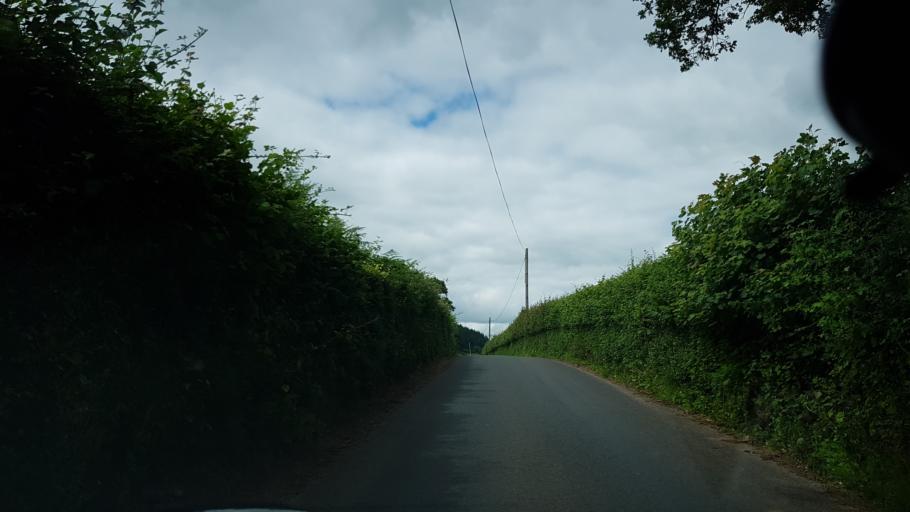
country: GB
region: Wales
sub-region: Monmouthshire
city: Grosmont
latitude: 51.8893
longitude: -2.8232
